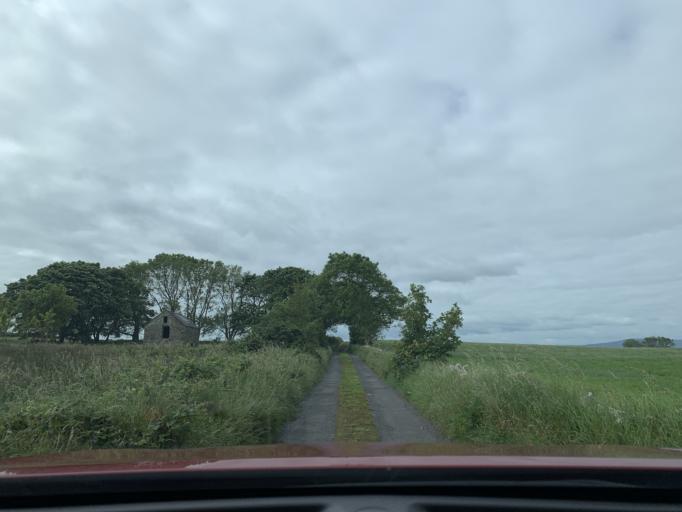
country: IE
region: Connaught
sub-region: Sligo
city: Sligo
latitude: 54.3667
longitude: -8.5207
